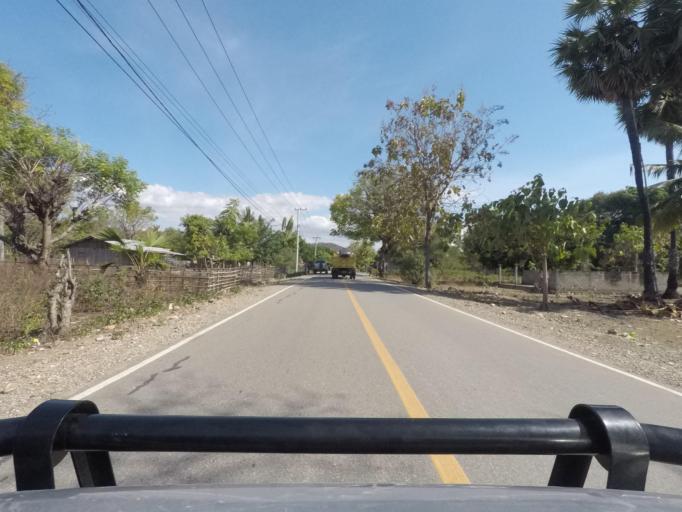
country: ID
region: East Nusa Tenggara
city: Atambua
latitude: -8.9418
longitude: 124.9784
